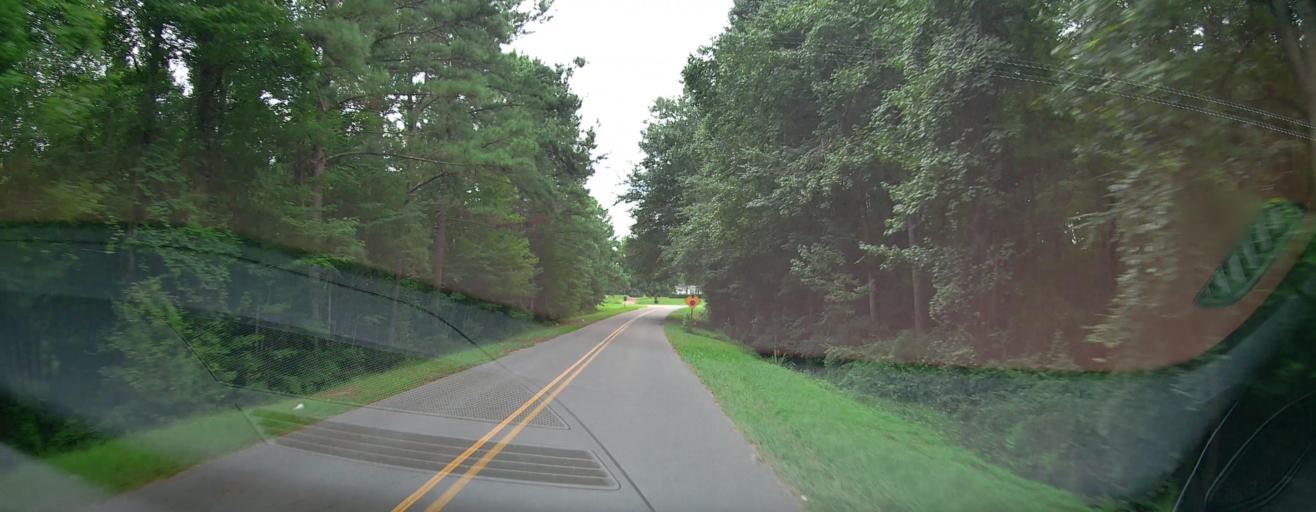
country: US
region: Georgia
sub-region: Schley County
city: Ellaville
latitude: 32.2184
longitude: -84.2867
